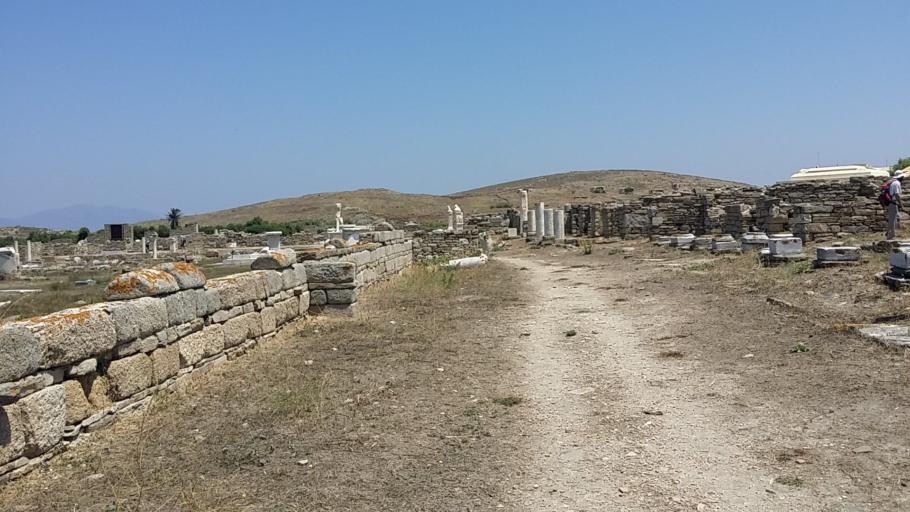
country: GR
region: South Aegean
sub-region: Nomos Kykladon
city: Mykonos
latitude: 37.4005
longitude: 25.2680
